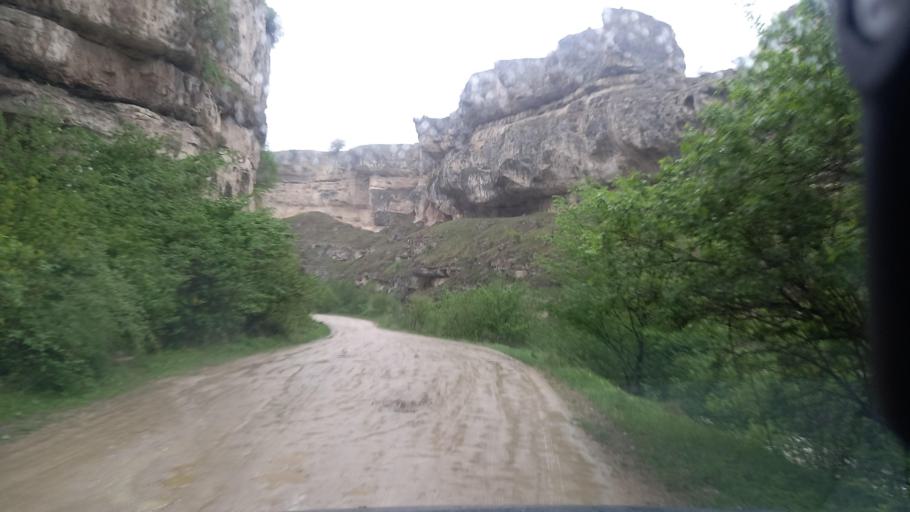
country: RU
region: Kabardino-Balkariya
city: Gundelen
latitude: 43.5970
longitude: 43.1466
